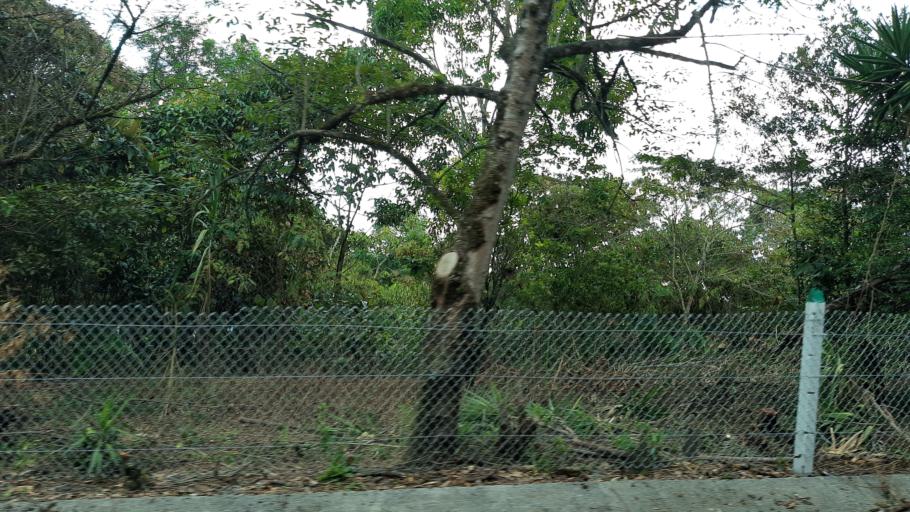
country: CO
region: Boyaca
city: Moniquira
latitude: 5.8567
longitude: -73.5766
